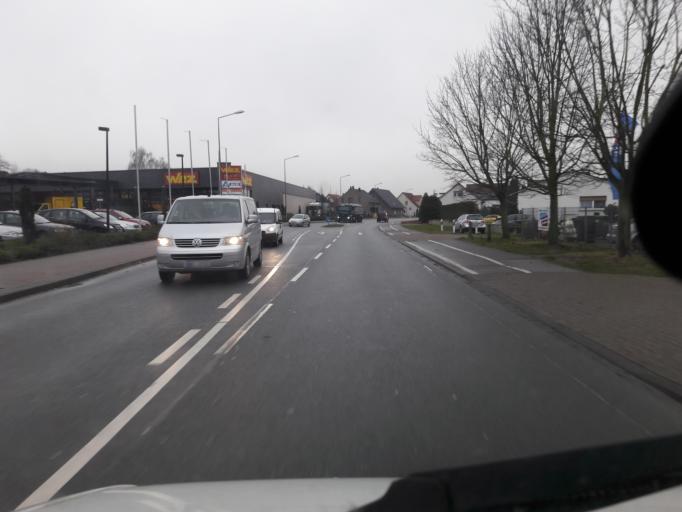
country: DE
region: North Rhine-Westphalia
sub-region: Regierungsbezirk Detmold
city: Minden
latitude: 52.2732
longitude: 8.8867
